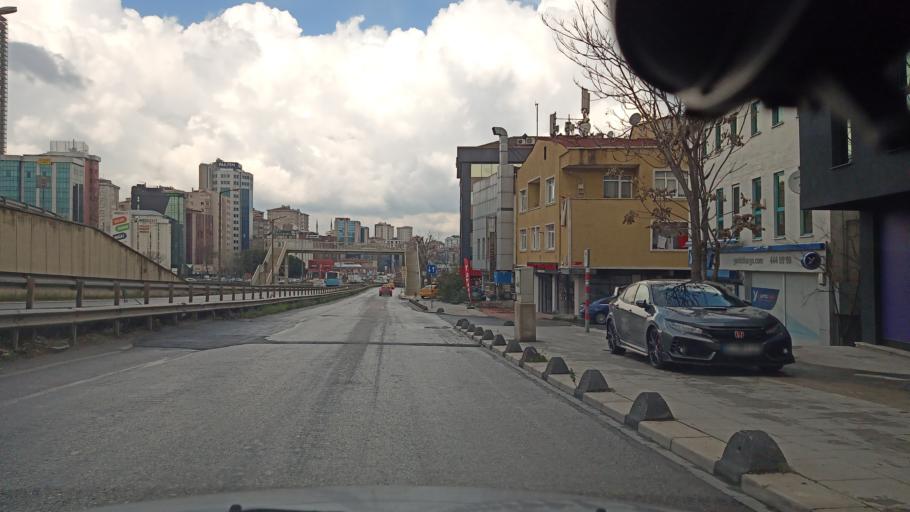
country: TR
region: Istanbul
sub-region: Atasehir
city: Atasehir
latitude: 40.9826
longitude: 29.0958
